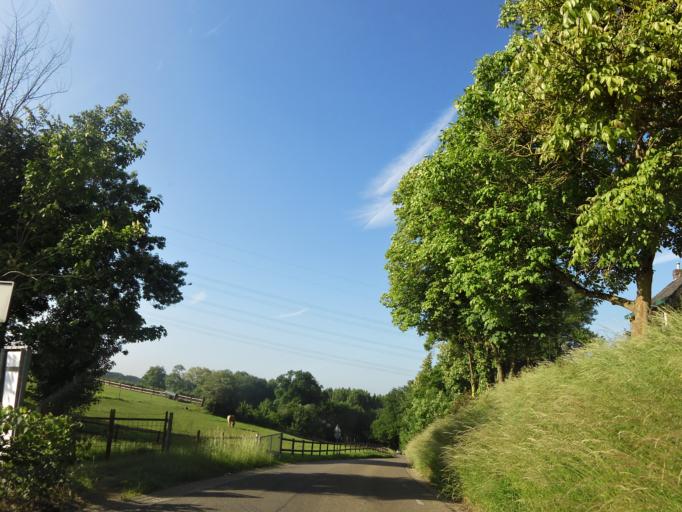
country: NL
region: Limburg
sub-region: Valkenburg aan de Geul
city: Broekhem
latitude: 50.8889
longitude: 5.8164
